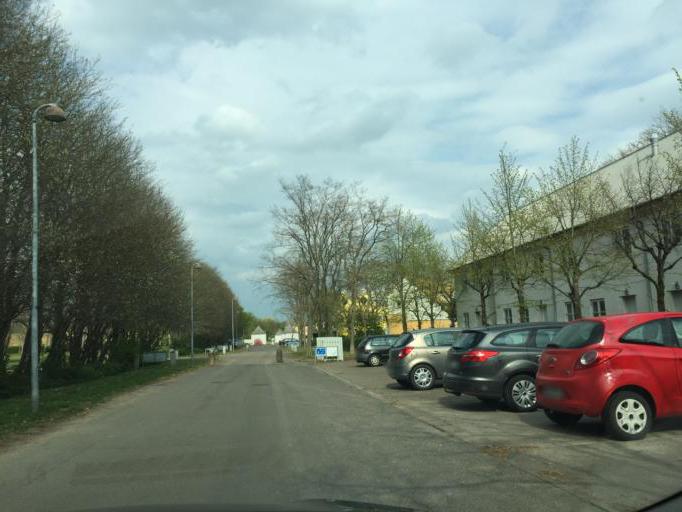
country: DK
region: South Denmark
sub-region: Odense Kommune
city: Neder Holluf
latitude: 55.3807
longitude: 10.4530
